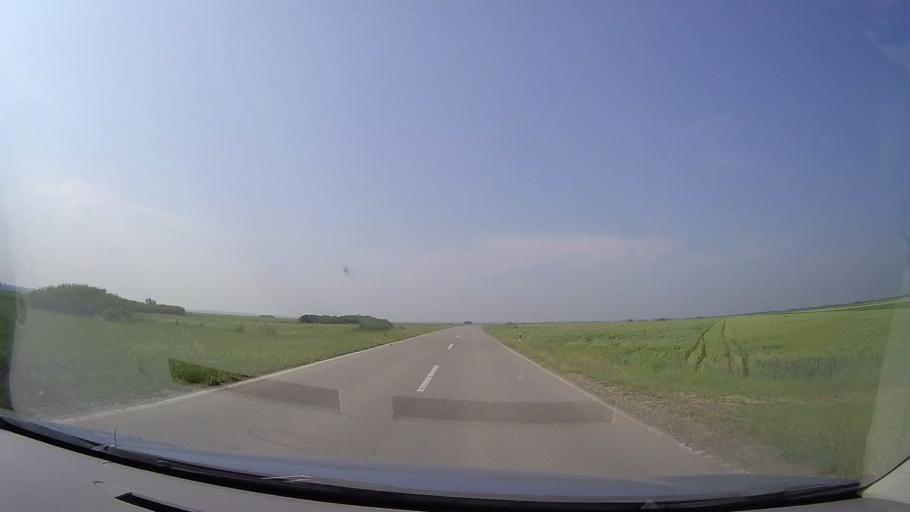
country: RS
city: Jasa Tomic
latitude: 45.4211
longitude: 20.8354
